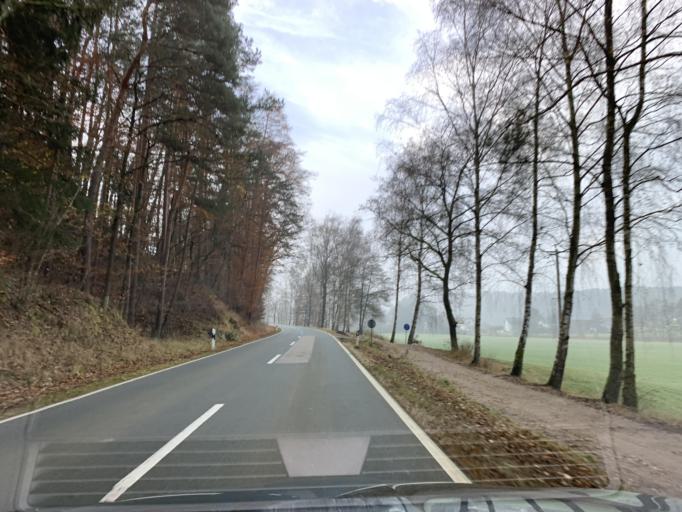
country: DE
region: Bavaria
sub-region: Upper Palatinate
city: Neunburg vorm Wald
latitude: 49.3675
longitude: 12.4025
